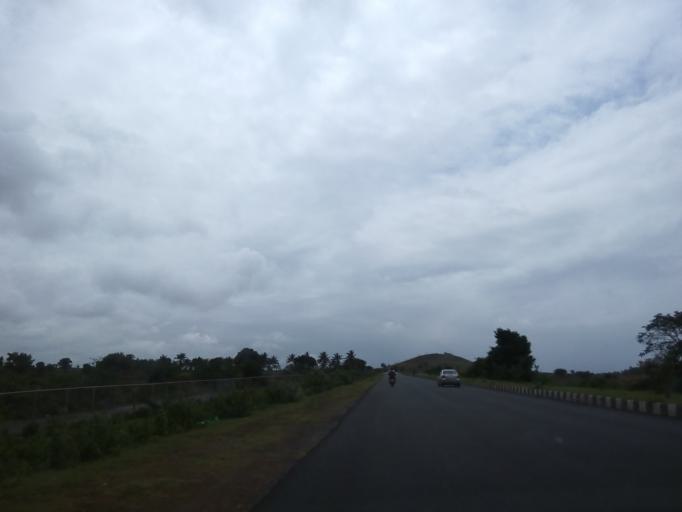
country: IN
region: Karnataka
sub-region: Haveri
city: Byadgi
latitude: 14.7161
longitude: 75.4956
